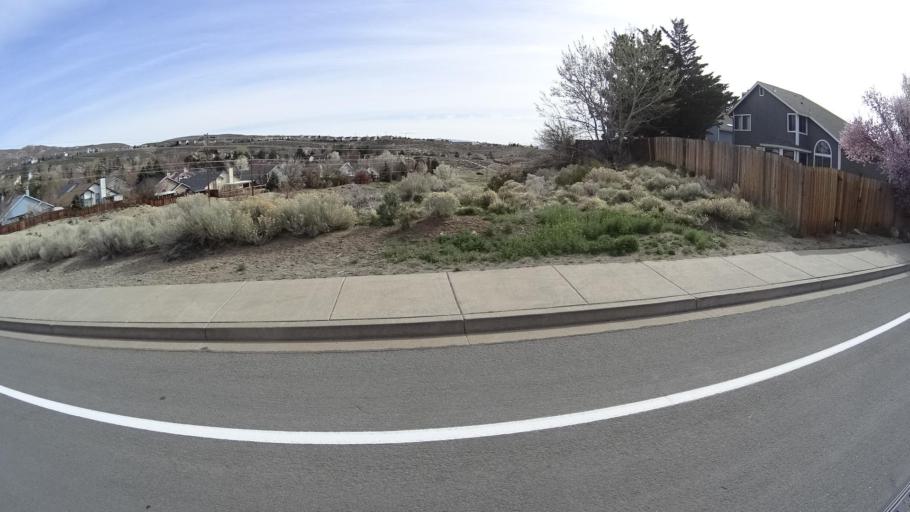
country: US
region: Nevada
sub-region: Washoe County
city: Mogul
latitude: 39.5326
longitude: -119.8949
